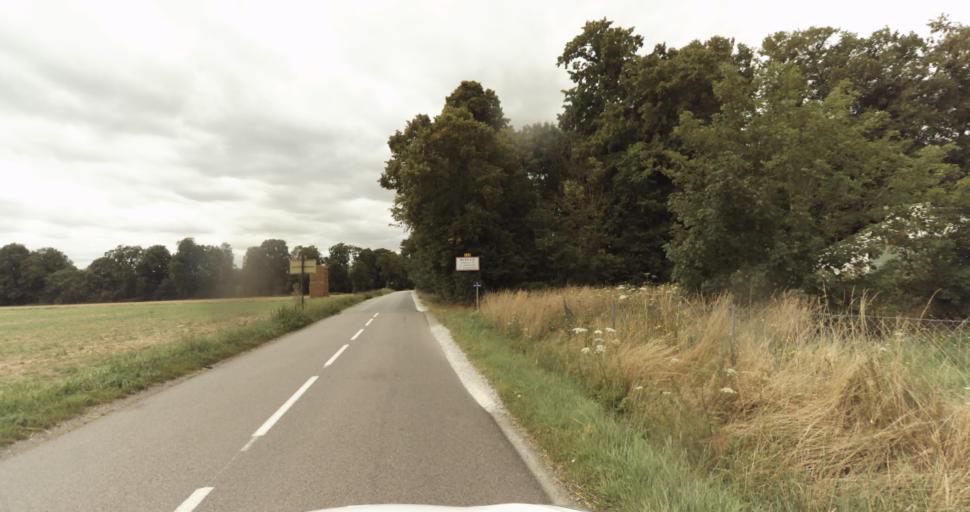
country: FR
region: Centre
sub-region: Departement d'Eure-et-Loir
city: Saint-Remy-sur-Avre
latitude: 48.7972
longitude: 1.2483
